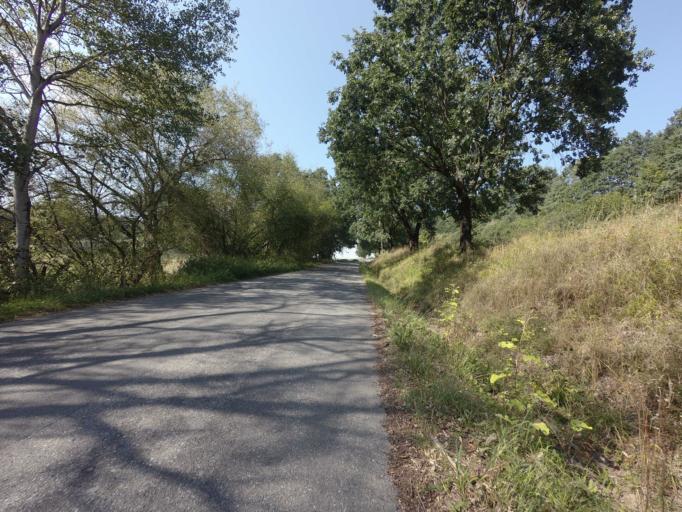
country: CZ
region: Jihocesky
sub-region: Okres Ceske Budejovice
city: Hluboka nad Vltavou
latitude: 49.1374
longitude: 14.4485
